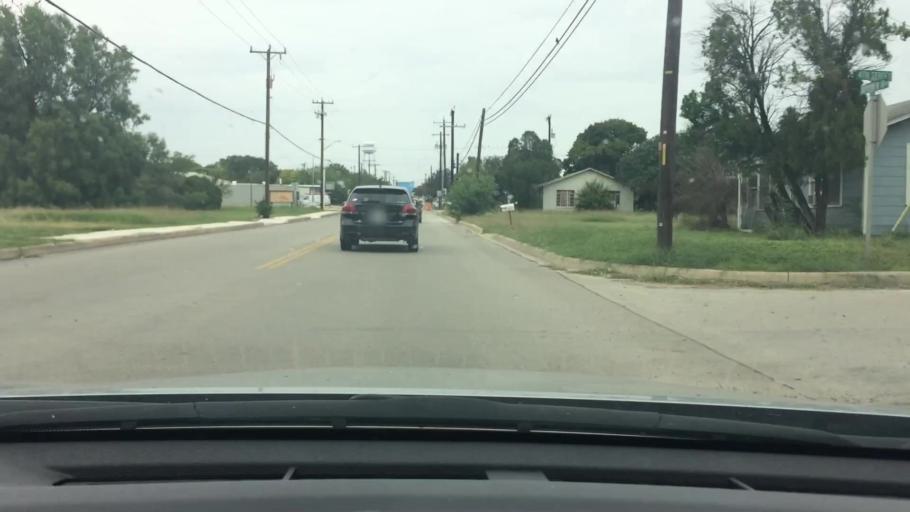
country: US
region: Texas
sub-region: Bexar County
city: Converse
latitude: 29.5215
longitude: -98.3188
